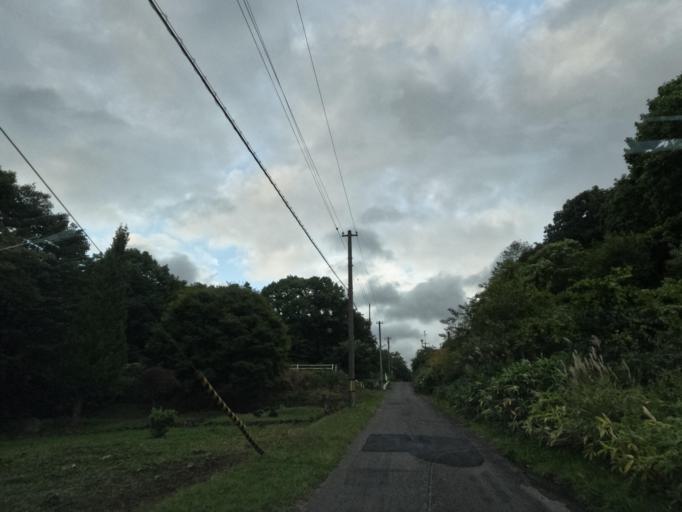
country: JP
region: Hokkaido
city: Muroran
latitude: 42.3674
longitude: 140.9655
